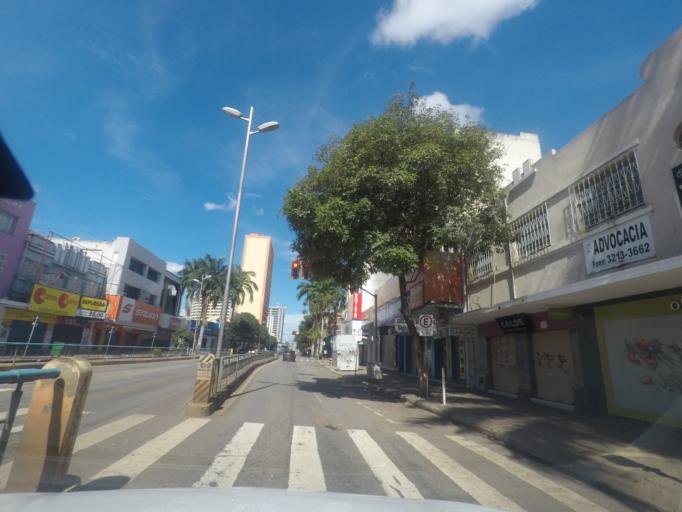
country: BR
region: Goias
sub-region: Goiania
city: Goiania
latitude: -16.6752
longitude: -49.2592
